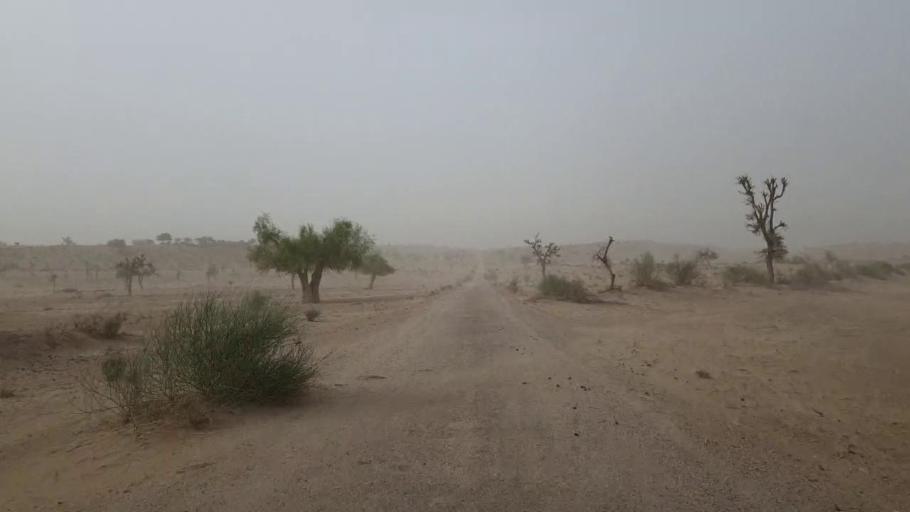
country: PK
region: Sindh
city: Islamkot
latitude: 24.5515
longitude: 70.3603
